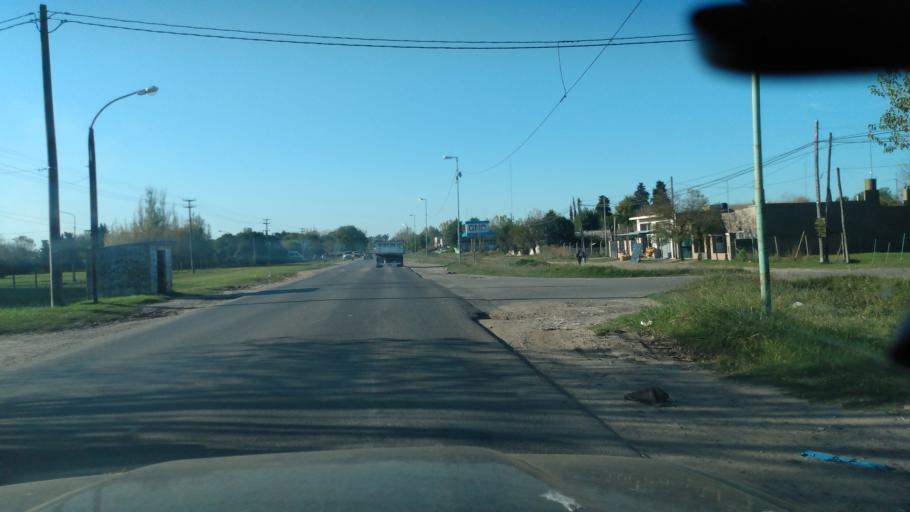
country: AR
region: Buenos Aires
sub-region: Partido de Lujan
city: Lujan
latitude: -34.5423
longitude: -59.1213
